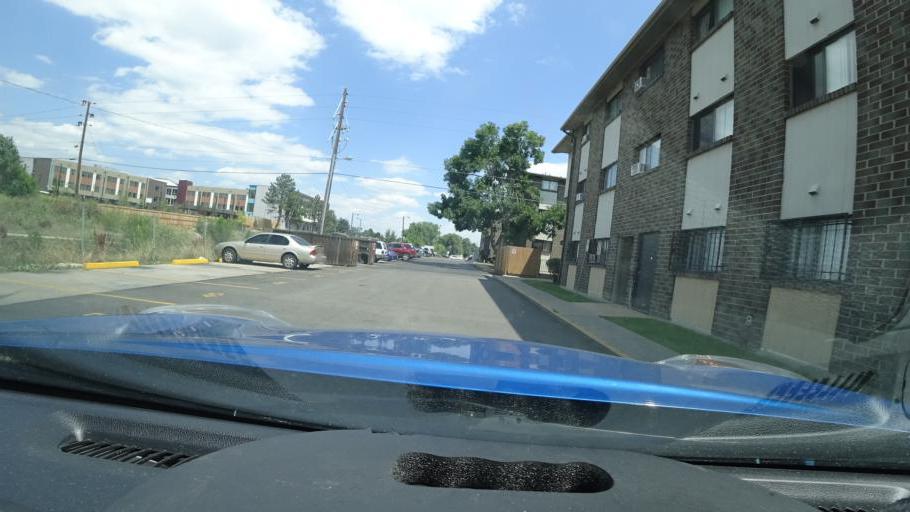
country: US
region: Colorado
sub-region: Arapahoe County
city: Sheridan
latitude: 39.6866
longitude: -105.0266
